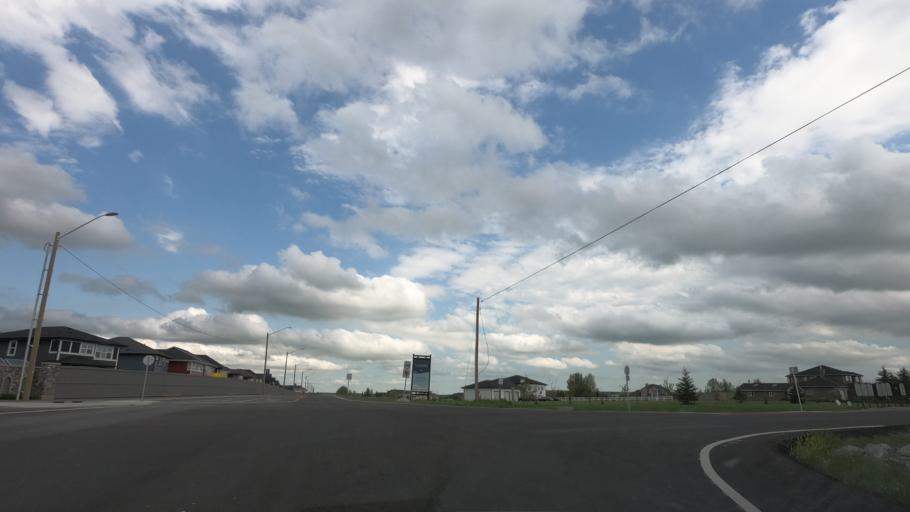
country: CA
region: Alberta
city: Airdrie
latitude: 51.2564
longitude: -113.9921
